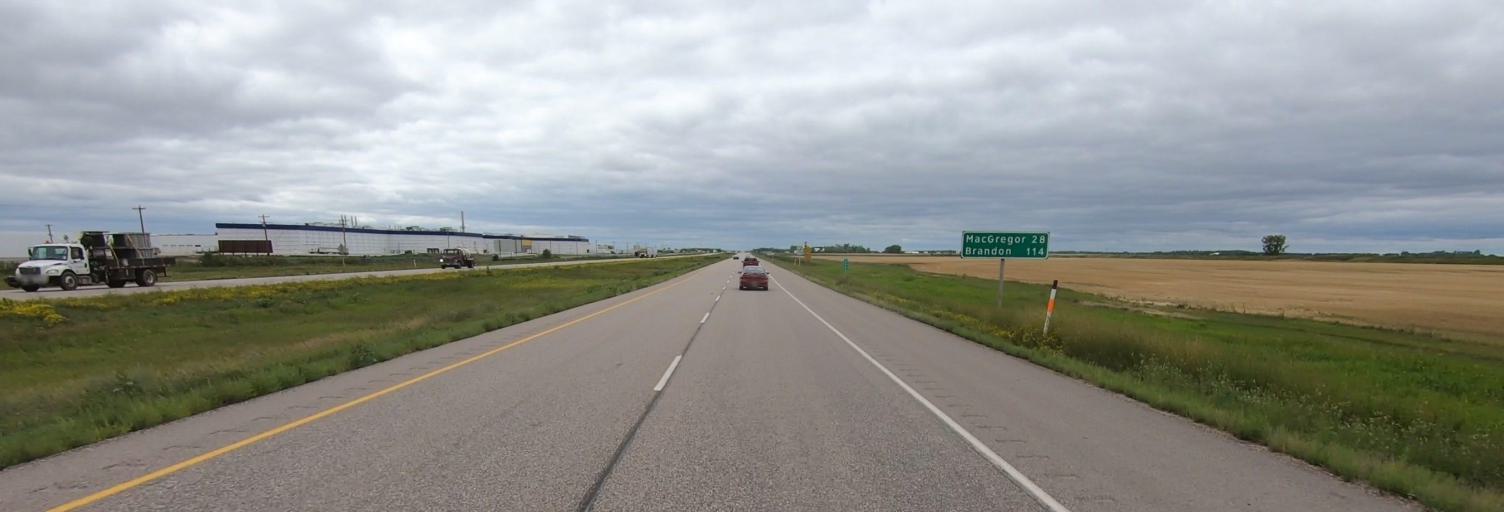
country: CA
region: Manitoba
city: Portage la Prairie
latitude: 49.9752
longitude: -98.3856
